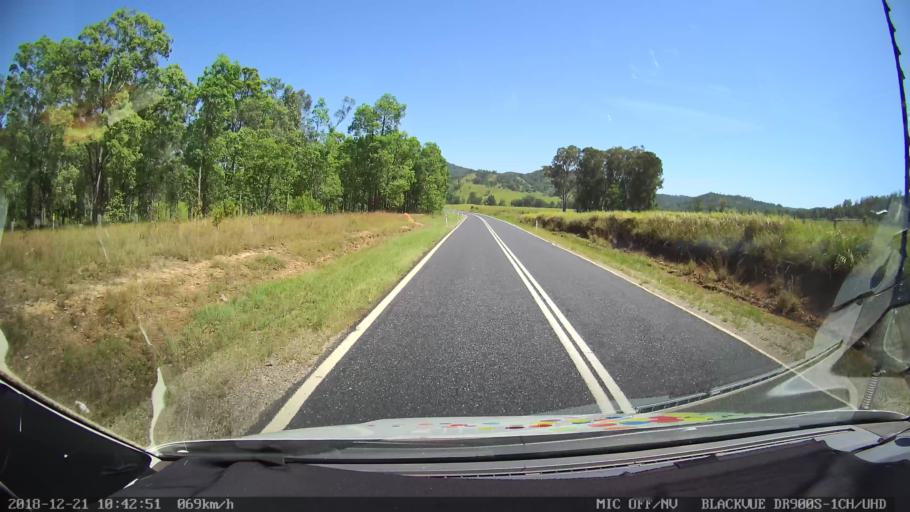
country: AU
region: New South Wales
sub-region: Clarence Valley
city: Gordon
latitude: -29.5810
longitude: 152.5606
